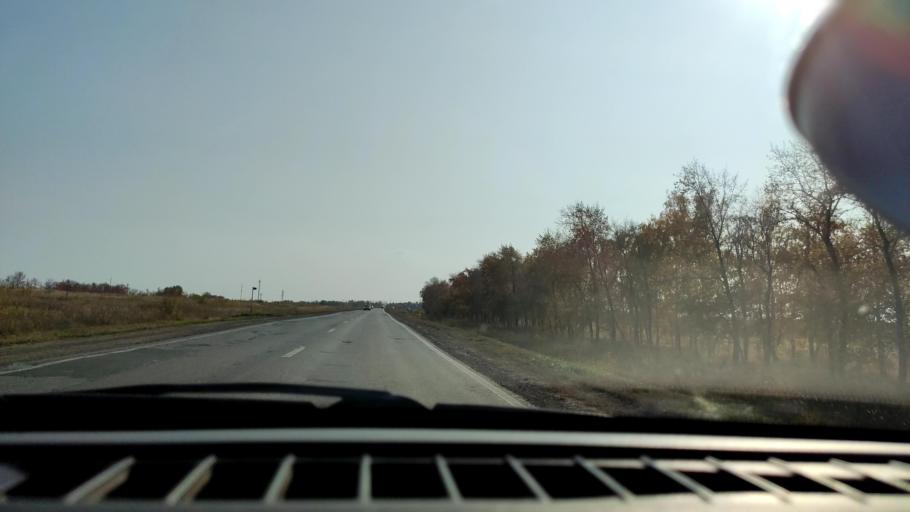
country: RU
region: Samara
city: Dubovyy Umet
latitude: 53.0911
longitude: 50.3494
